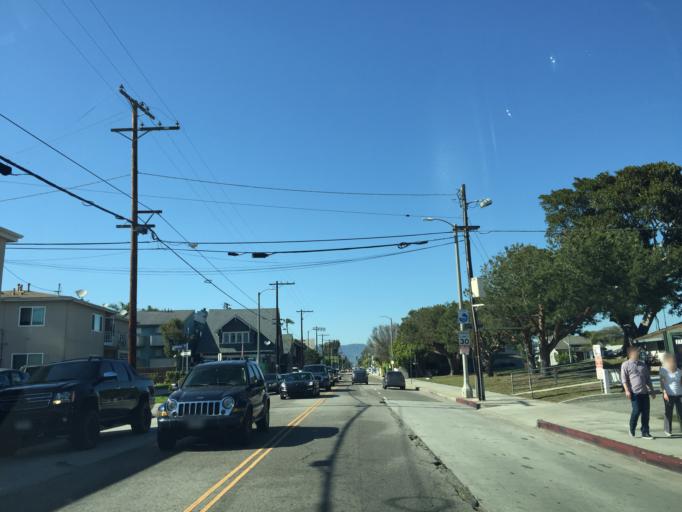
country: US
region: California
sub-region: Los Angeles County
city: Marina del Rey
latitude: 33.9894
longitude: -118.4737
